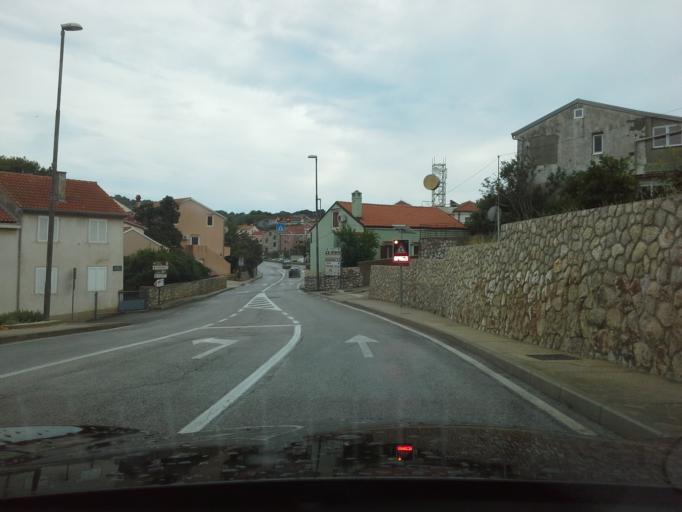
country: HR
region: Primorsko-Goranska
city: Mali Losinj
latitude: 44.5306
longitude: 14.4767
